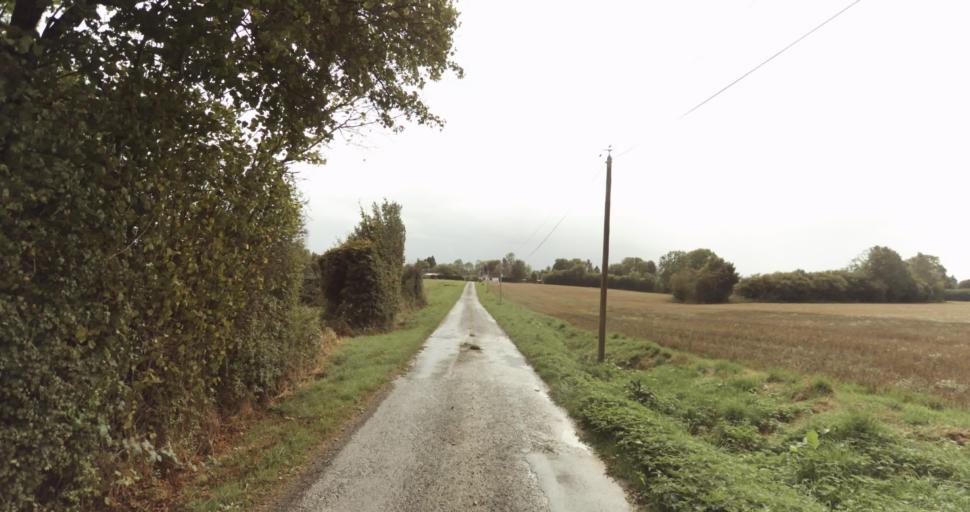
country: FR
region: Lower Normandy
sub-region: Departement de l'Orne
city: Sainte-Gauburge-Sainte-Colombe
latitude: 48.6865
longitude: 0.4106
